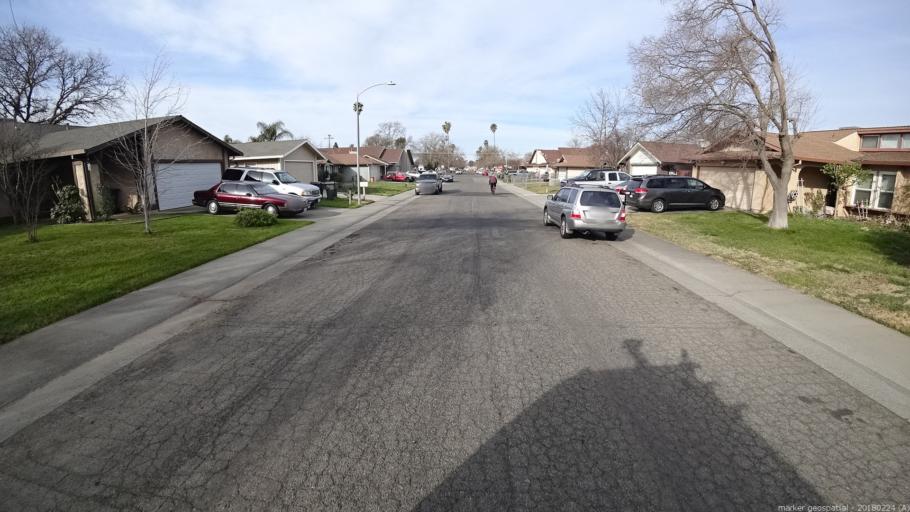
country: US
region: California
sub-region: Sacramento County
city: Rio Linda
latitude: 38.6863
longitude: -121.4605
